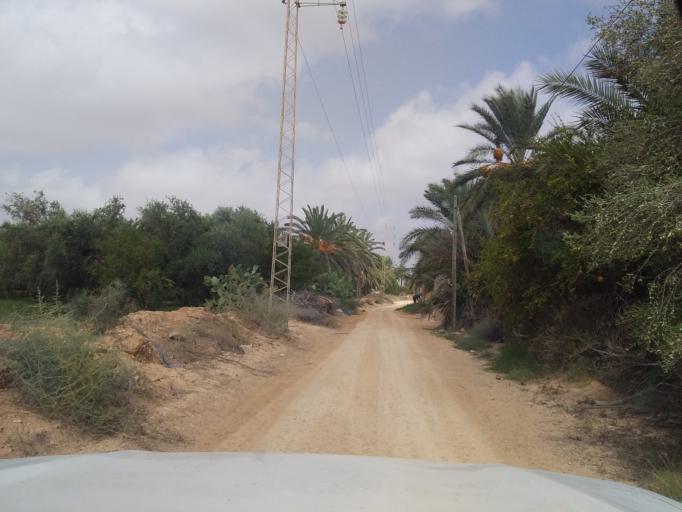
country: TN
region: Madanin
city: Medenine
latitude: 33.6245
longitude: 10.3119
